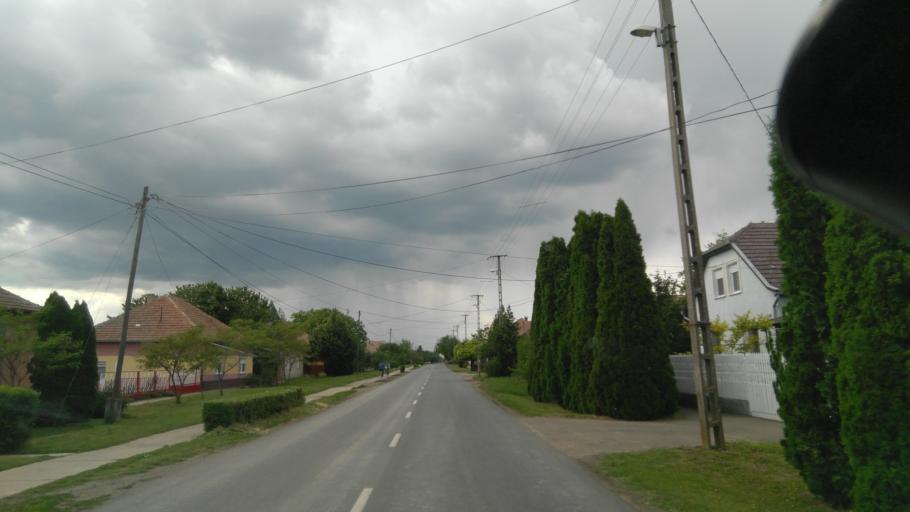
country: HU
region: Bekes
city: Dombegyhaz
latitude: 46.3440
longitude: 21.1265
